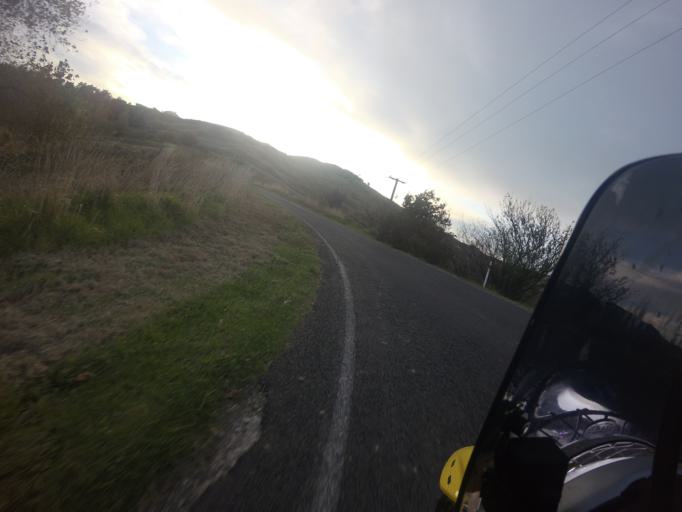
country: NZ
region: Gisborne
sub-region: Gisborne District
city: Gisborne
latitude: -38.6635
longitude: 178.0625
